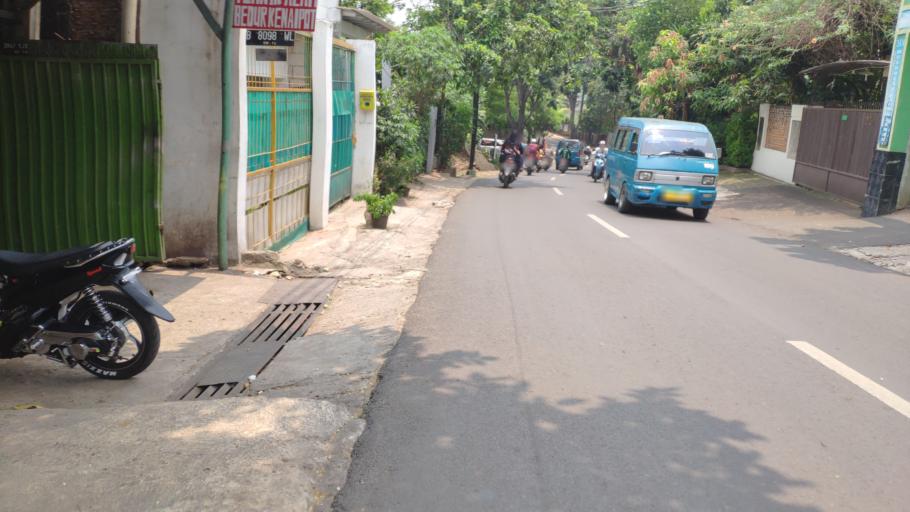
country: ID
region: West Java
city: Depok
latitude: -6.3505
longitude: 106.8045
